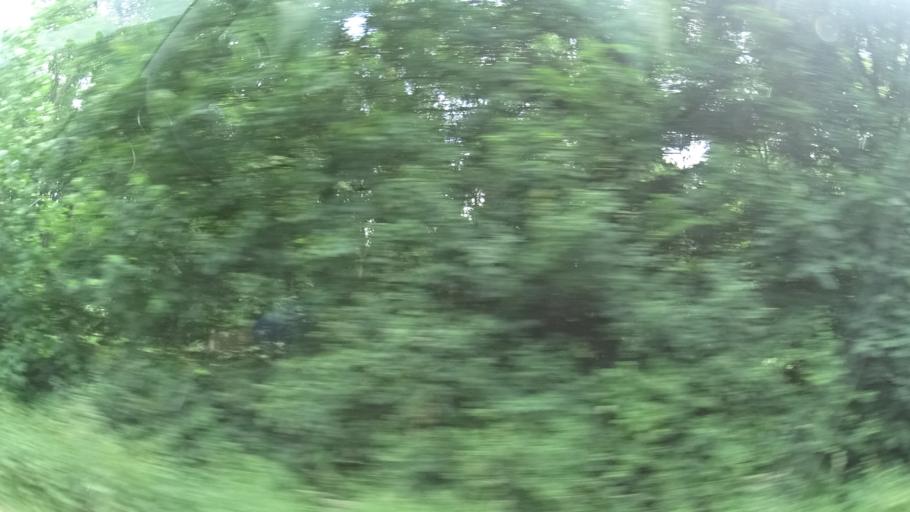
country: DE
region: Lower Saxony
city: Springe
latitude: 52.1759
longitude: 9.6144
